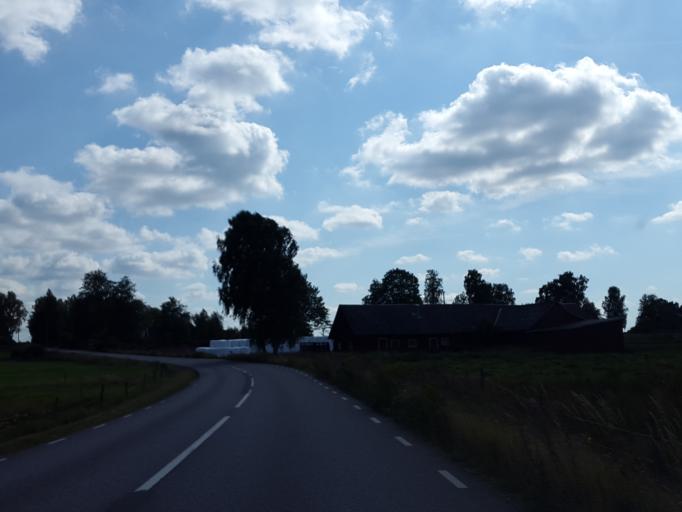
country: SE
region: Vaestra Goetaland
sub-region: Herrljunga Kommun
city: Herrljunga
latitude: 58.0722
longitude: 13.0715
